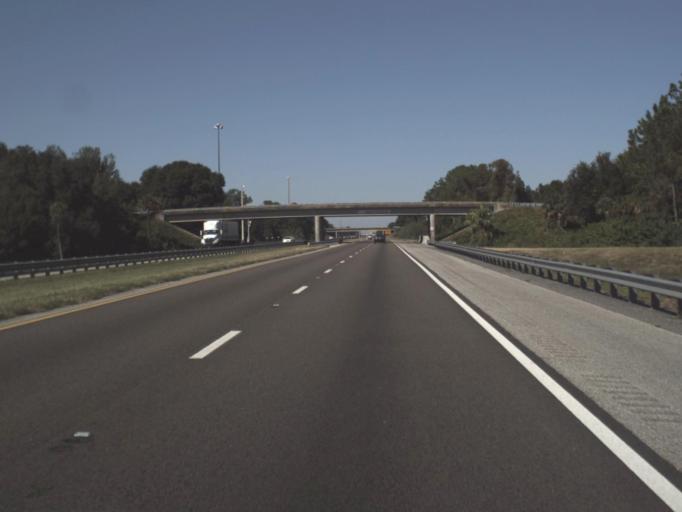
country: US
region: Florida
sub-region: Lake County
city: Howie In The Hills
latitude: 28.6511
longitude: -81.8054
